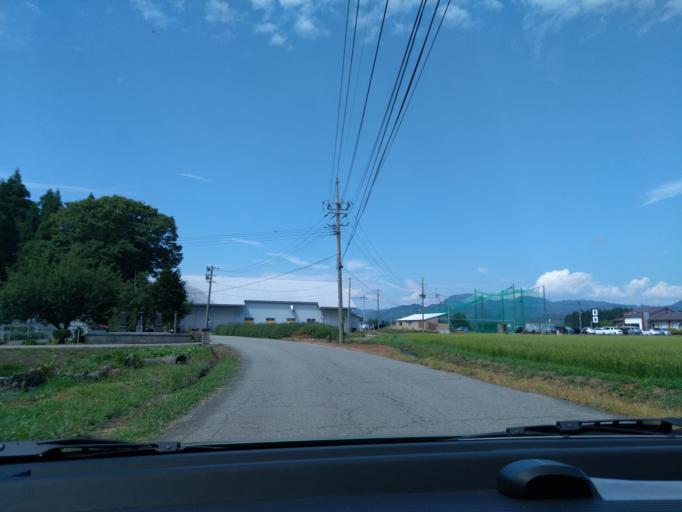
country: JP
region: Akita
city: Kakunodatemachi
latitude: 39.6118
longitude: 140.5946
